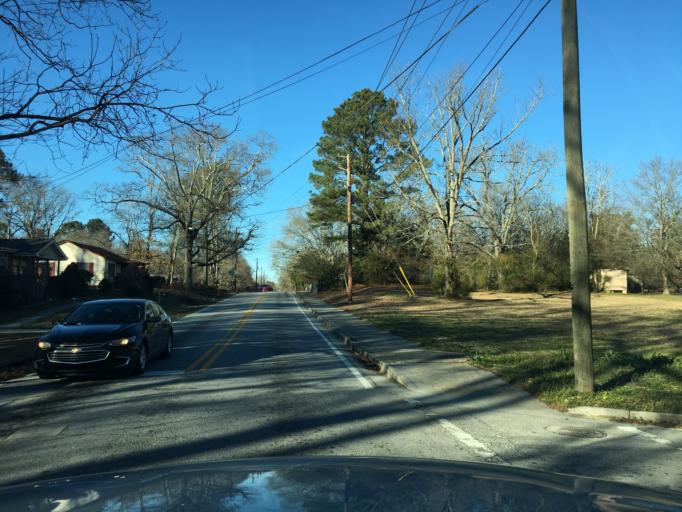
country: US
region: Georgia
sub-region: Rockdale County
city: Conyers
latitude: 33.6758
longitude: -84.0297
